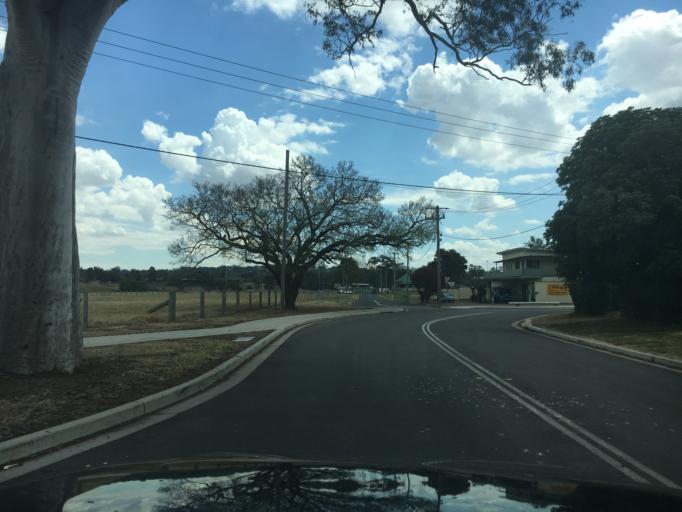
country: AU
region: New South Wales
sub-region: Singleton
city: Singleton
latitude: -32.5599
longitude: 151.1671
